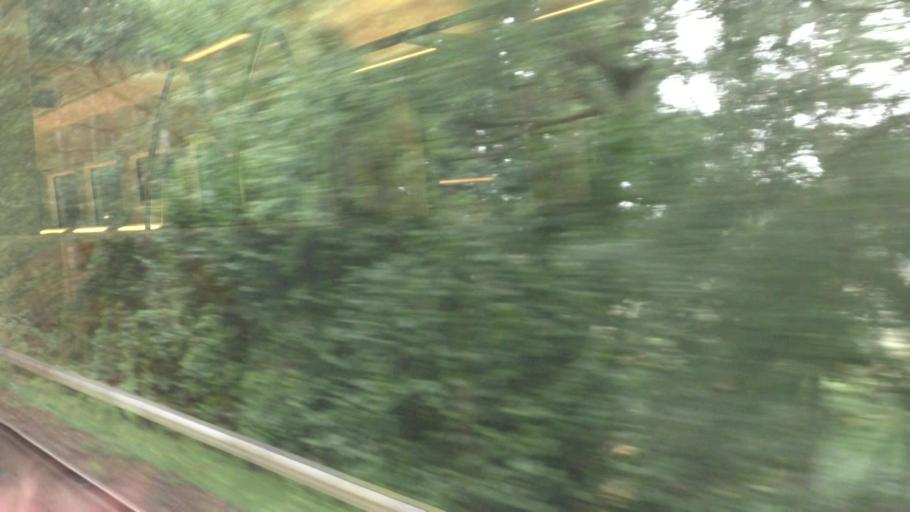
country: DE
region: Saxony
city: Arnsdorf
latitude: 51.0946
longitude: 14.0201
